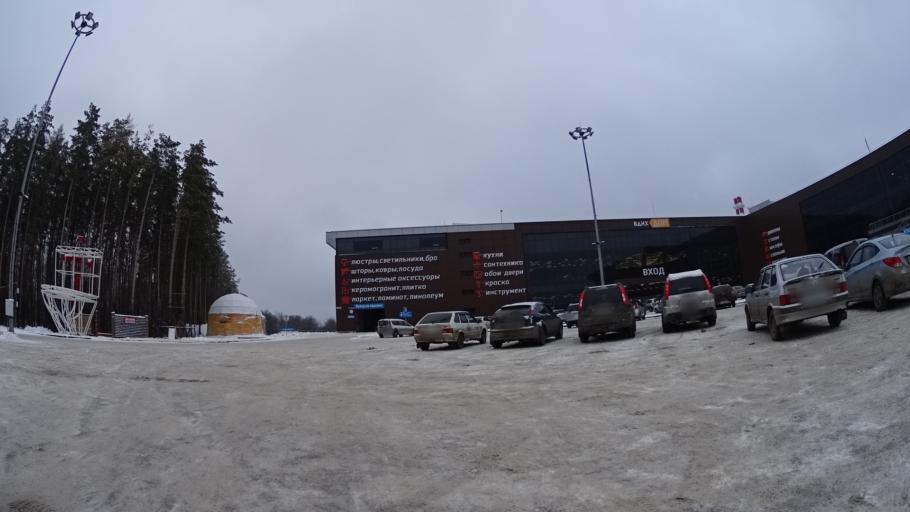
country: RU
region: Bashkortostan
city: Ufa
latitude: 54.7253
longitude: 56.0193
